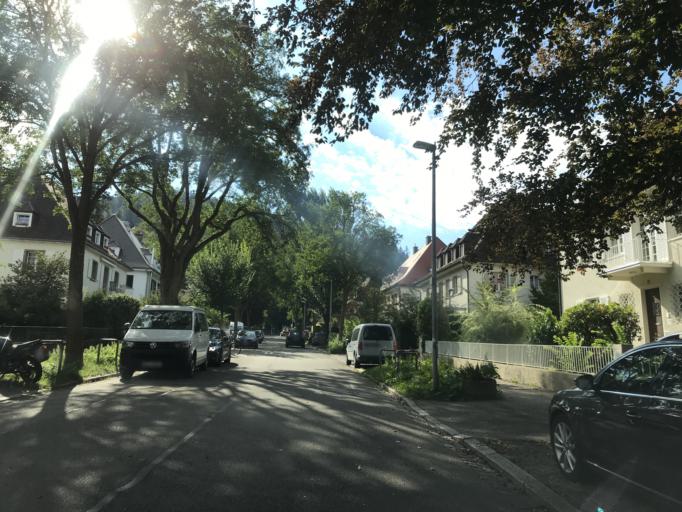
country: DE
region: Baden-Wuerttemberg
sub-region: Freiburg Region
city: Freiburg
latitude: 47.9806
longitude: 7.8459
